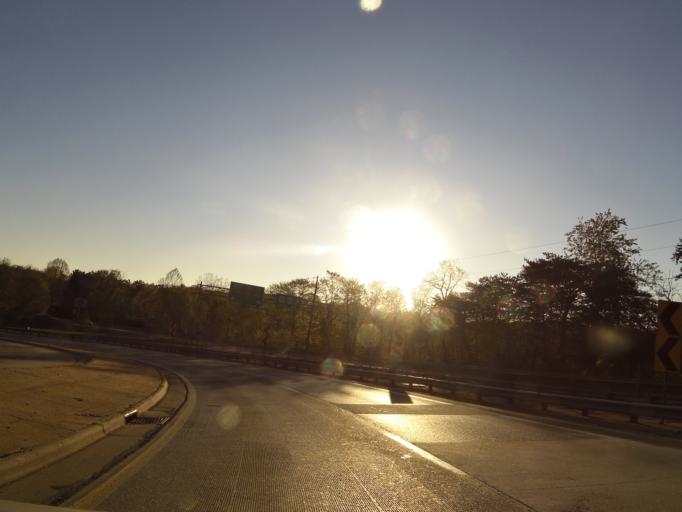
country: US
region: North Carolina
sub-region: Buncombe County
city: Asheville
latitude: 35.5902
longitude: -82.5791
